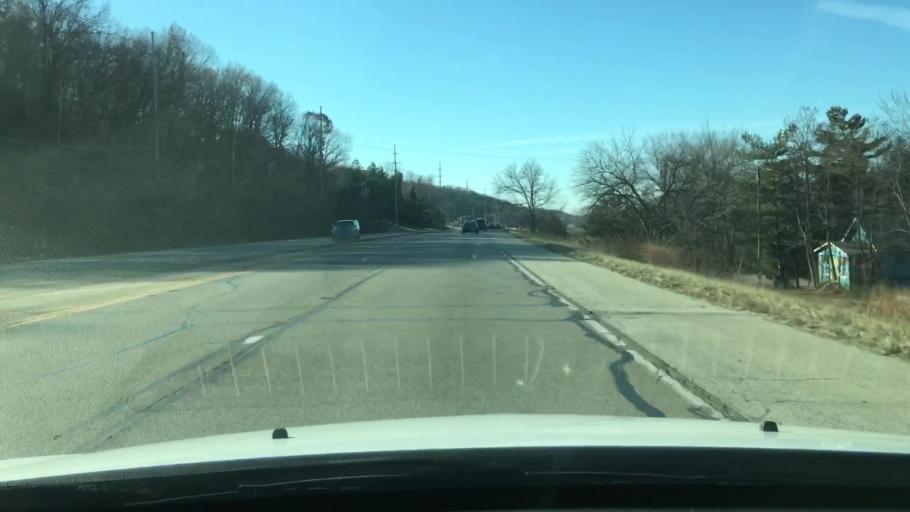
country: US
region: Illinois
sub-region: Tazewell County
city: East Peoria
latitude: 40.6811
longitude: -89.5562
